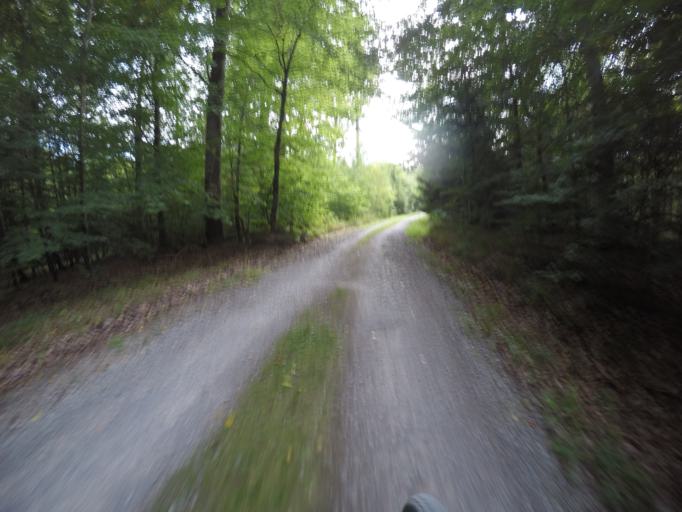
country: DE
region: Baden-Wuerttemberg
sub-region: Regierungsbezirk Stuttgart
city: Gerlingen
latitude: 48.7583
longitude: 9.0506
